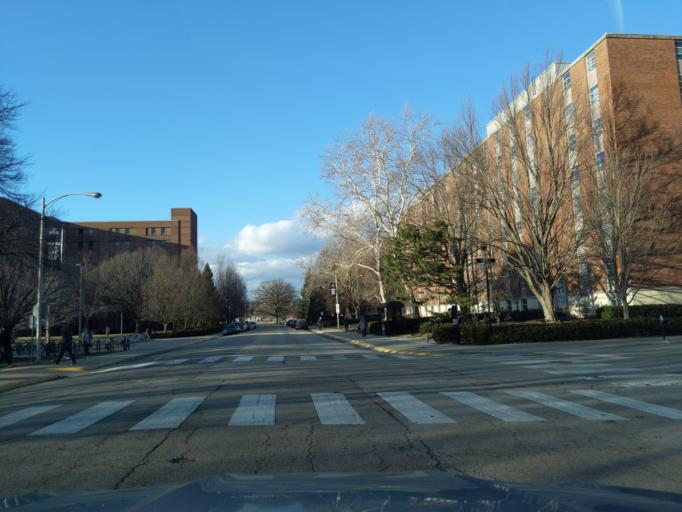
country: US
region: Indiana
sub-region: Tippecanoe County
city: West Lafayette
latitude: 40.4252
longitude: -86.9257
